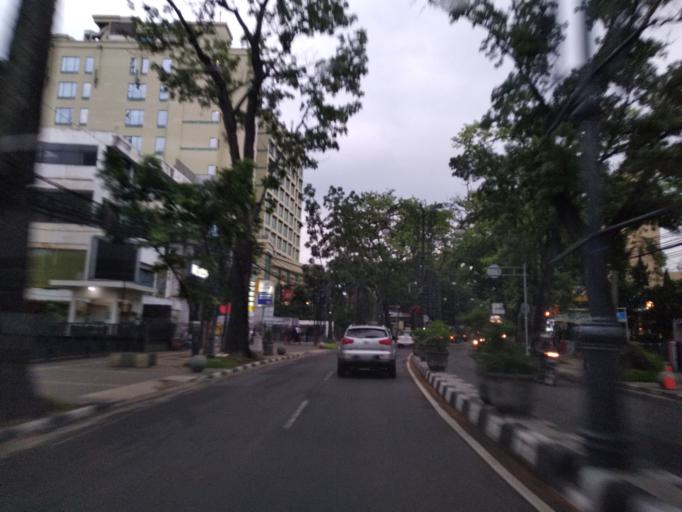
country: ID
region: West Java
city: Bandung
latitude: -6.9053
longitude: 107.6106
